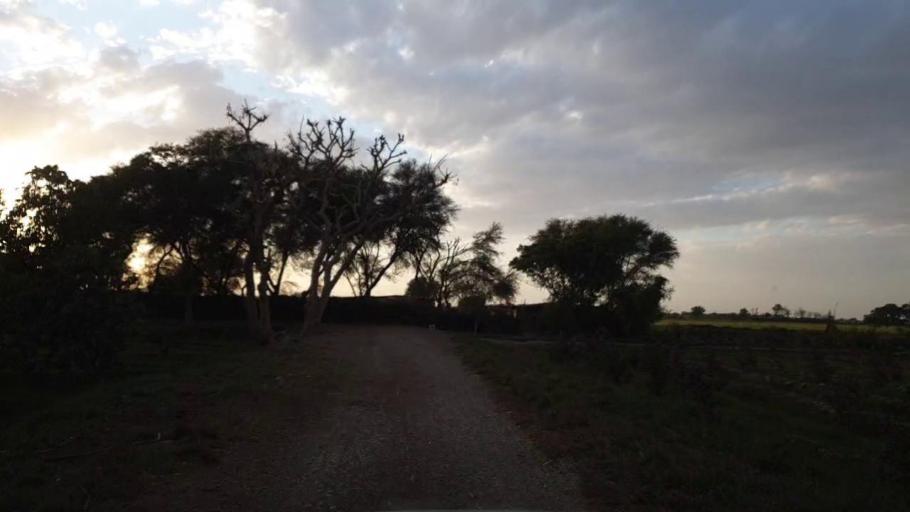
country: PK
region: Sindh
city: Matiari
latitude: 25.5803
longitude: 68.4371
